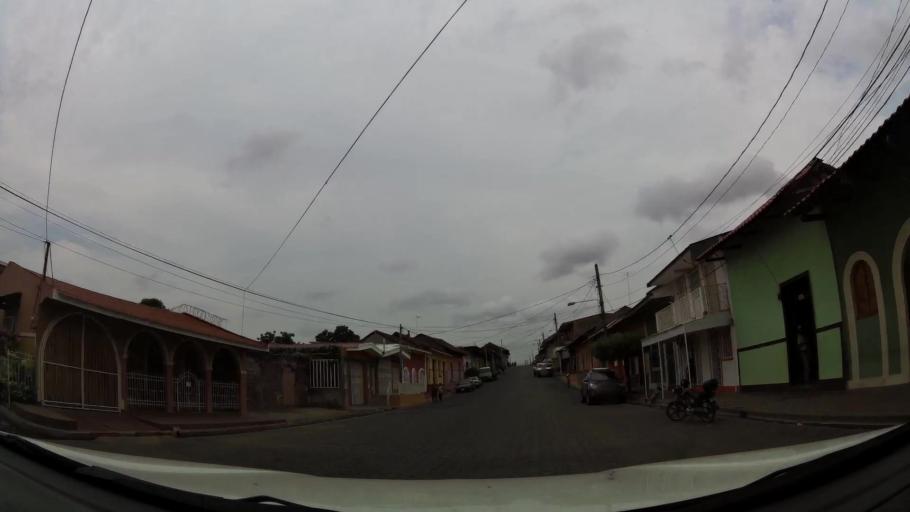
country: NI
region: Granada
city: Granada
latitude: 11.9277
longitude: -85.9589
